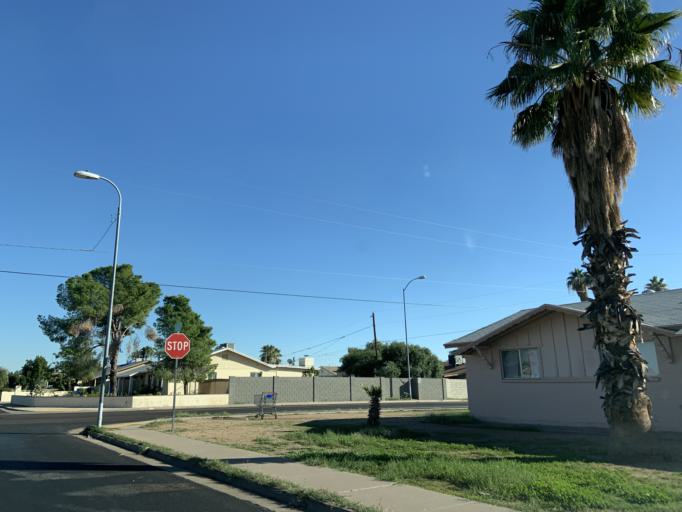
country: US
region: Arizona
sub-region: Maricopa County
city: Tempe
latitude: 33.4050
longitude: -111.8660
